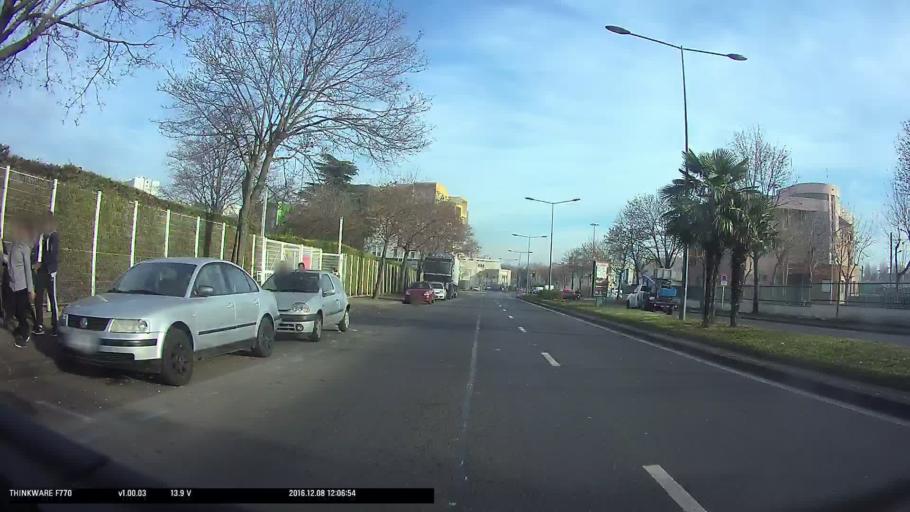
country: FR
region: Ile-de-France
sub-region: Departement de Seine-Saint-Denis
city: Bobigny
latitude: 48.9014
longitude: 2.4432
